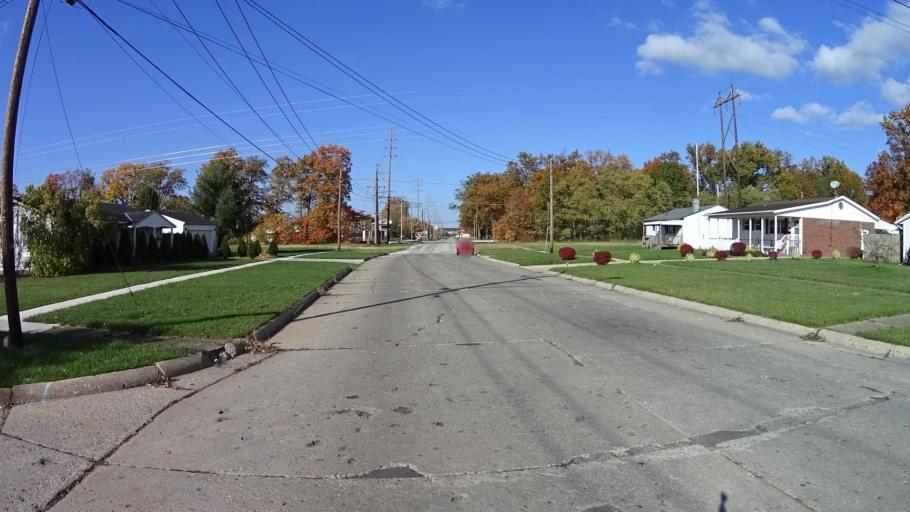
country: US
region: Ohio
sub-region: Lorain County
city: Sheffield
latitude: 41.4369
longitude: -82.1276
